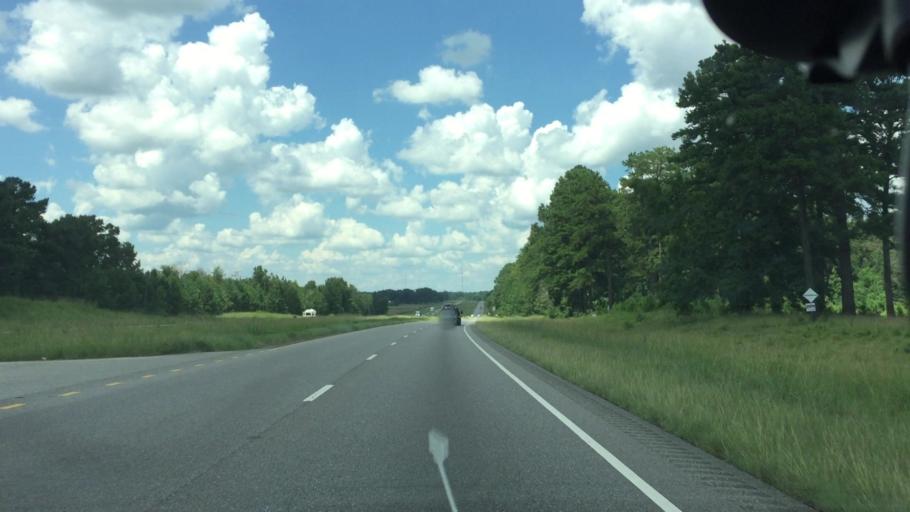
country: US
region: Alabama
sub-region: Montgomery County
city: Taylor
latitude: 32.0203
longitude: -86.0311
